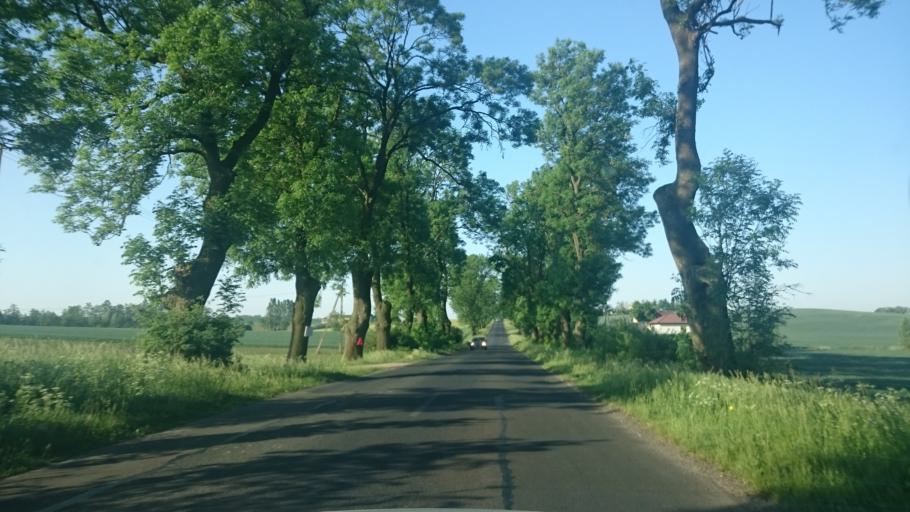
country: PL
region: Kujawsko-Pomorskie
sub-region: Powiat golubsko-dobrzynski
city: Zbojno
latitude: 52.9921
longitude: 19.1250
